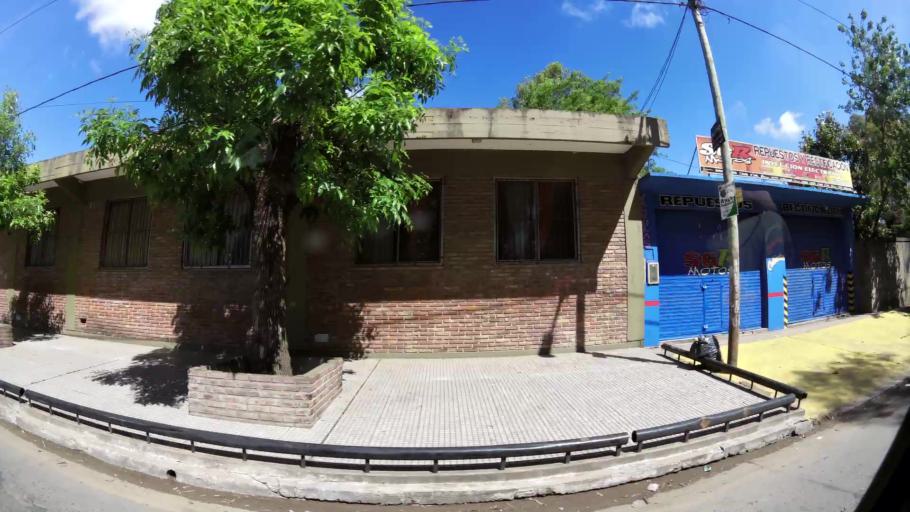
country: AR
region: Buenos Aires
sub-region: Partido de Quilmes
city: Quilmes
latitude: -34.8117
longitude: -58.2634
